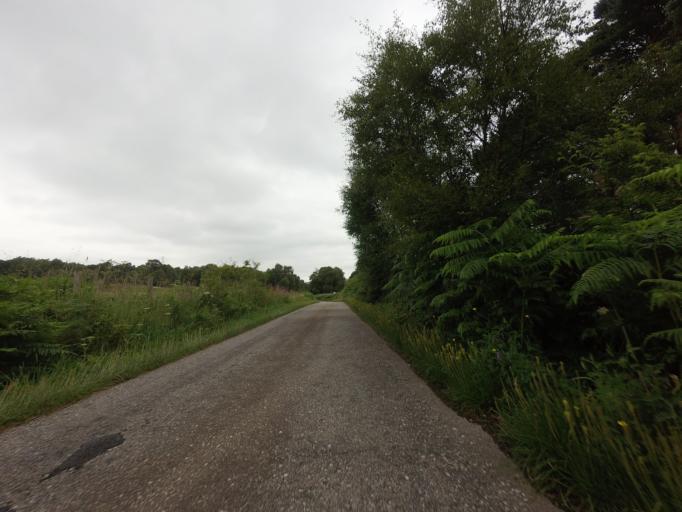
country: GB
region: Scotland
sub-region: Highland
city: Evanton
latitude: 57.9045
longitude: -4.3891
